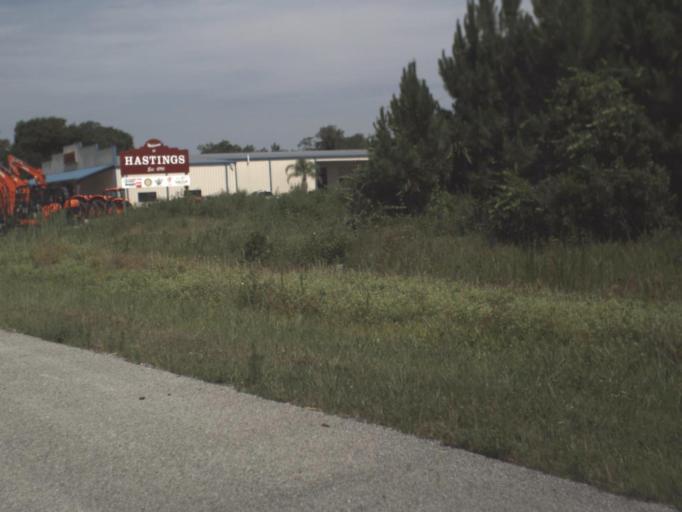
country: US
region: Florida
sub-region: Putnam County
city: East Palatka
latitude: 29.7146
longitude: -81.4981
